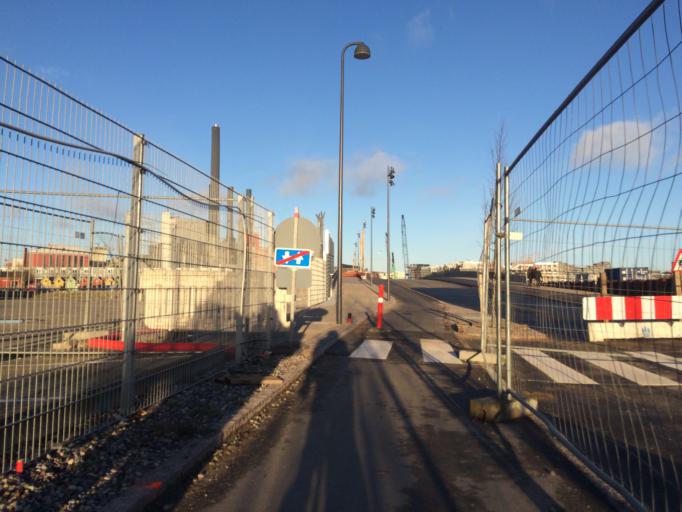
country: DK
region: Capital Region
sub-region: Kobenhavn
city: Copenhagen
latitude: 55.6524
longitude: 12.5552
